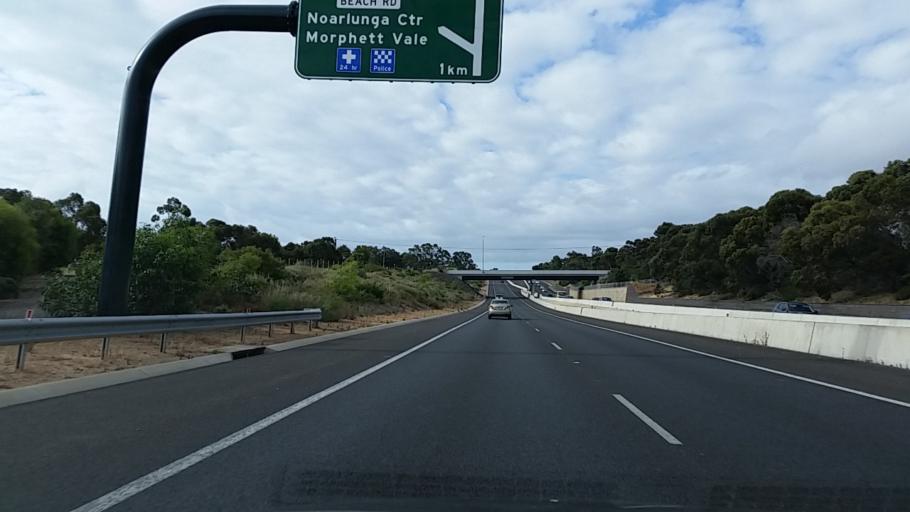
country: AU
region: South Australia
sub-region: Onkaparinga
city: Noarlunga Downs
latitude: -35.1504
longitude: 138.5056
